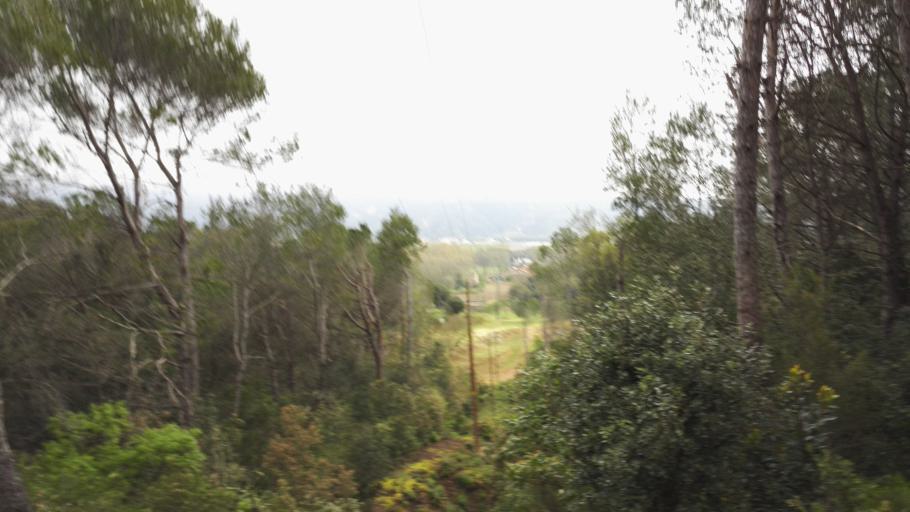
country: ES
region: Catalonia
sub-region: Provincia de Barcelona
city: Santa Maria de Palautordera
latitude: 41.7062
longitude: 2.4166
